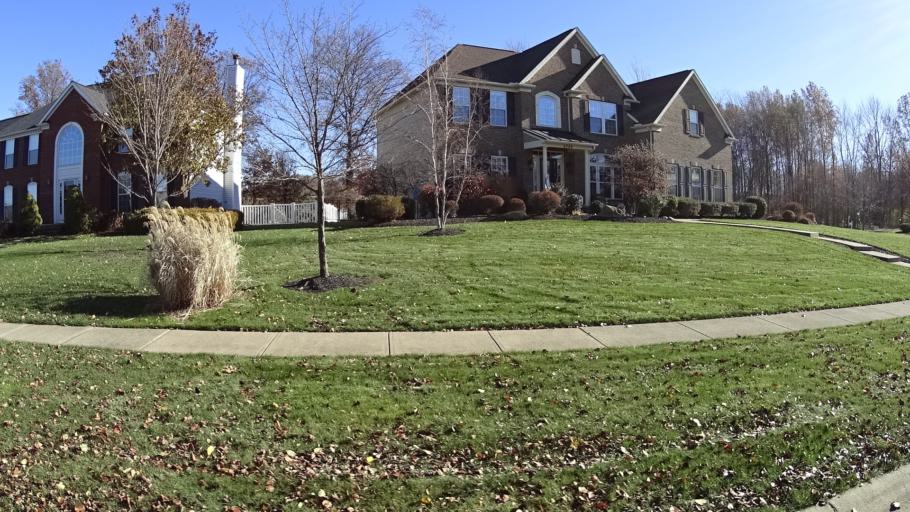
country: US
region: Ohio
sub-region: Lorain County
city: Avon
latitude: 41.4197
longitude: -82.0514
